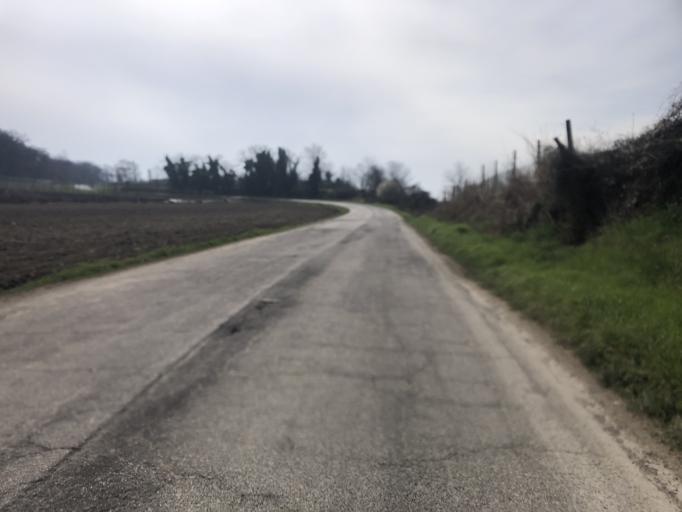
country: IT
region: Veneto
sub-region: Provincia di Verona
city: San Giorgio in Salici
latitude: 45.4123
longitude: 10.7740
